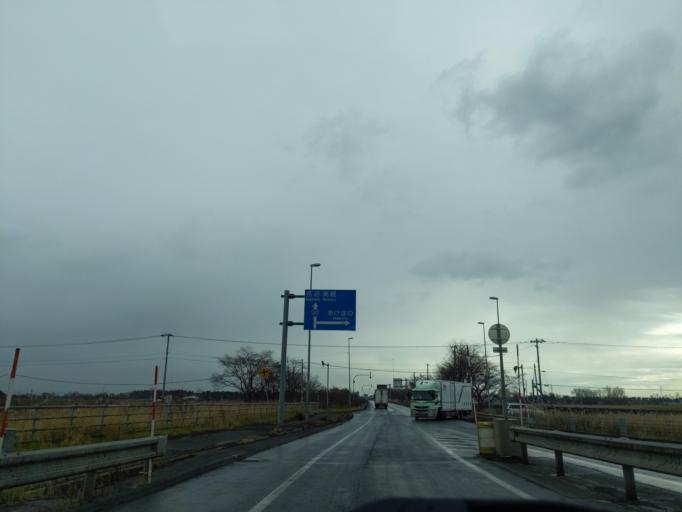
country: JP
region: Hokkaido
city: Ebetsu
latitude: 43.1124
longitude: 141.5894
